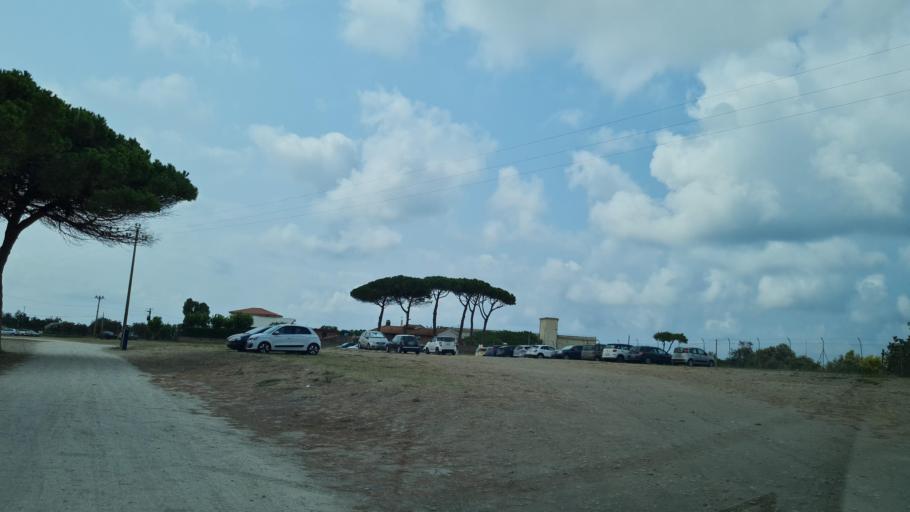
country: IT
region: Latium
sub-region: Provincia di Viterbo
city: Tarquinia
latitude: 42.2140
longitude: 11.7107
